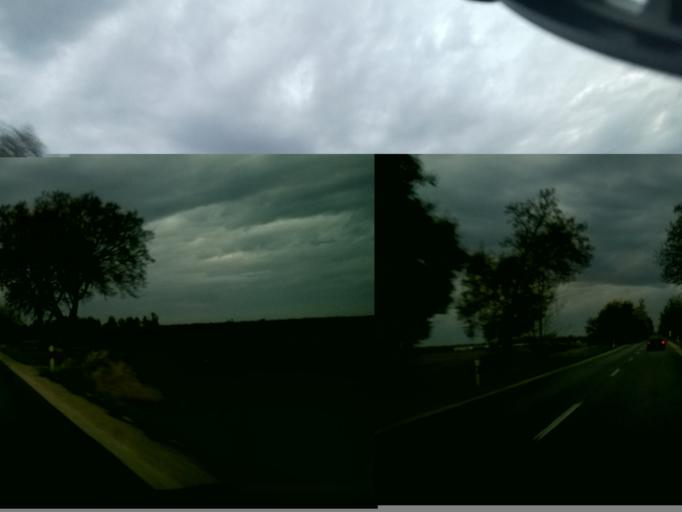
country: HU
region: Pest
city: Domsod
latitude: 47.0622
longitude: 19.0162
